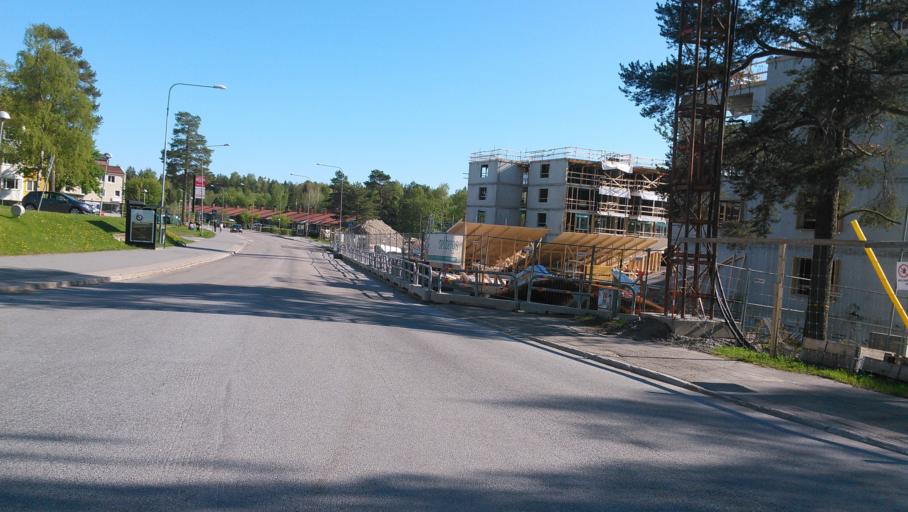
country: SE
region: Vaesterbotten
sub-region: Umea Kommun
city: Umea
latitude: 63.8265
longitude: 20.2941
